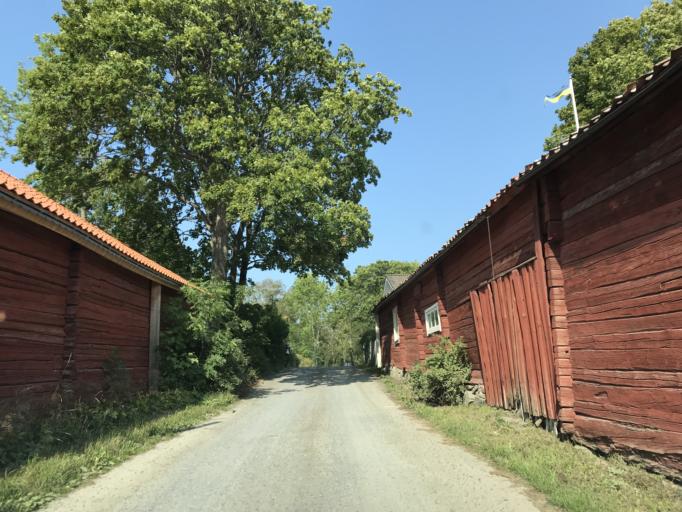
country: SE
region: Stockholm
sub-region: Norrtalje Kommun
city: Bjorko
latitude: 59.8478
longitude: 19.0140
